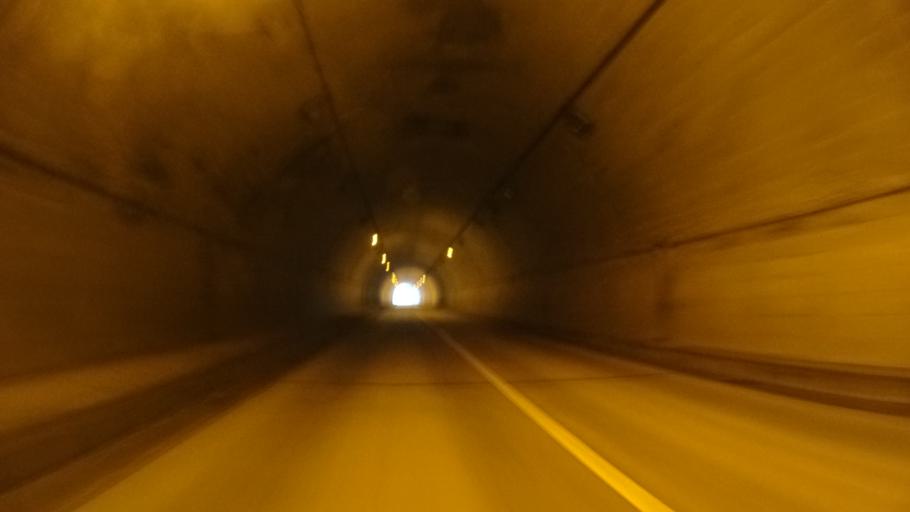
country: JP
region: Ishikawa
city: Hakui
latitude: 37.0823
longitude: 136.7308
